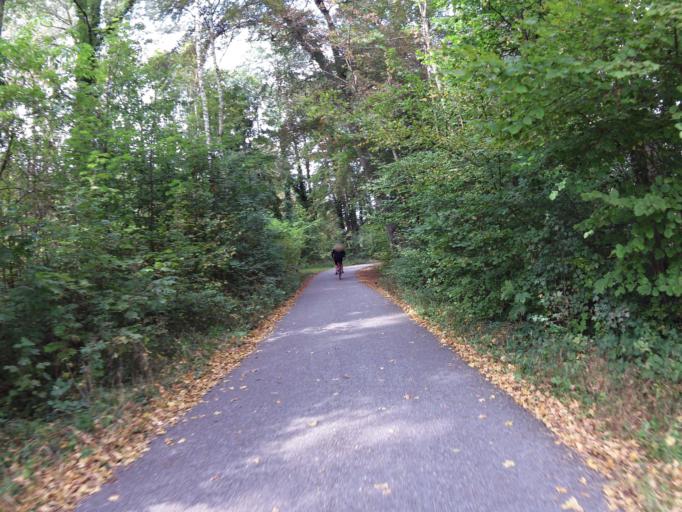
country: DE
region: Bavaria
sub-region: Upper Bavaria
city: Bernried
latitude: 47.8616
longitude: 11.3005
